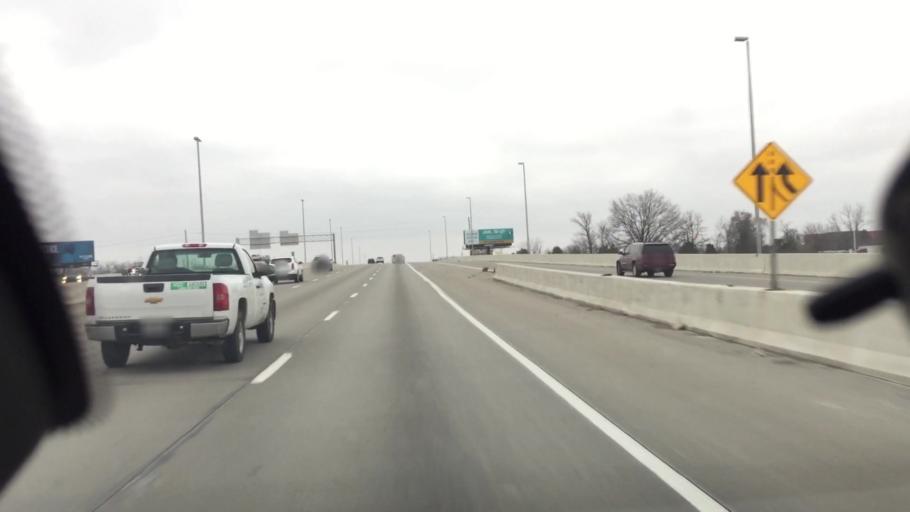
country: US
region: Indiana
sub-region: Marion County
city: Speedway
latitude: 39.7458
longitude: -86.2648
